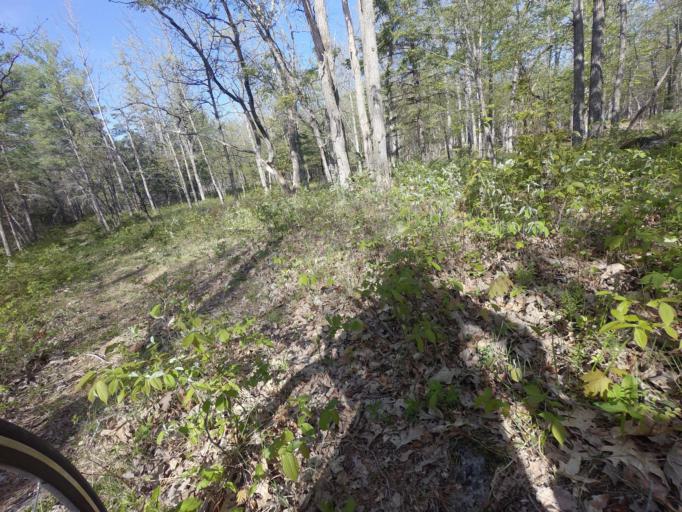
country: CA
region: Ontario
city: Arnprior
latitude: 45.4690
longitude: -76.2996
